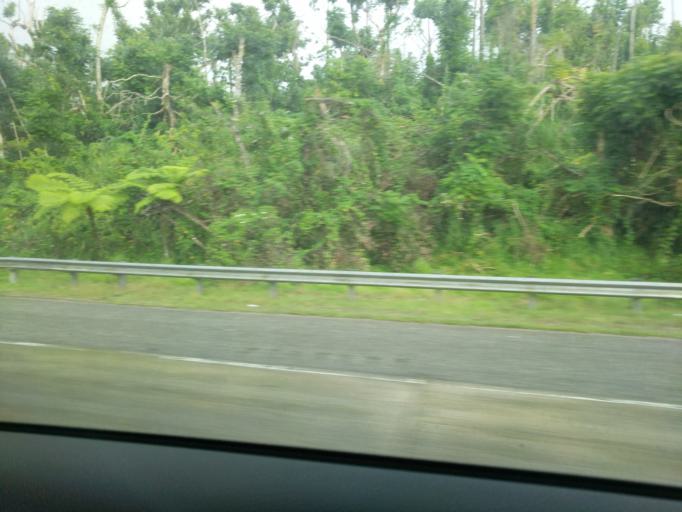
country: PR
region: Cidra
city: Bayamon
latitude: 18.1614
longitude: -66.0913
